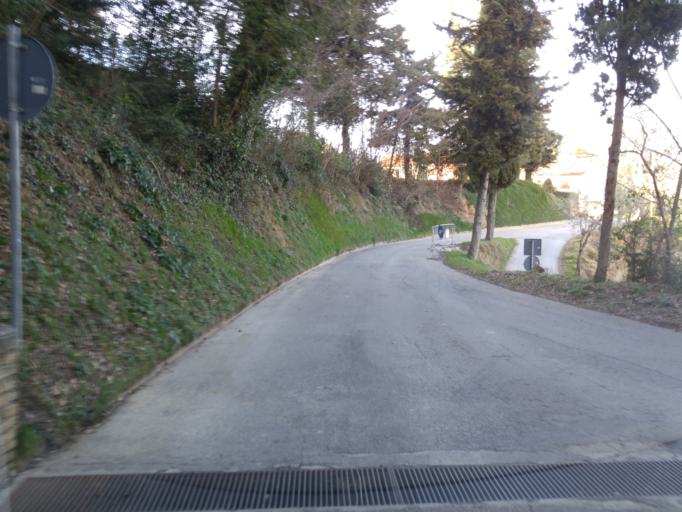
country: IT
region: The Marches
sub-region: Provincia di Pesaro e Urbino
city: Cartoceto
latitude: 43.7633
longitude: 12.8828
